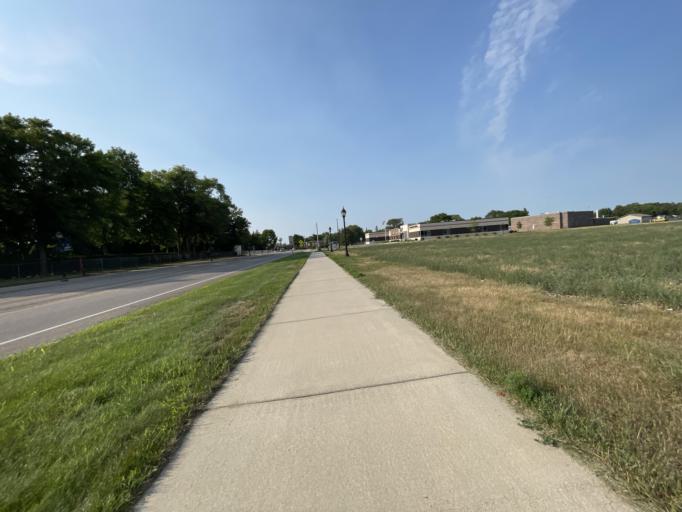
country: US
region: Minnesota
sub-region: Stearns County
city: Saint Joseph
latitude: 45.5607
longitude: -94.3167
